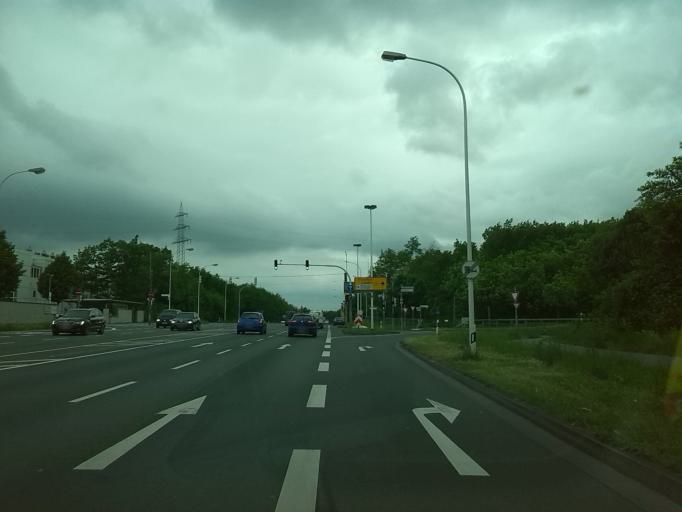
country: DE
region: Hesse
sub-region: Regierungsbezirk Darmstadt
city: Darmstadt
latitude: 49.8906
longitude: 8.6289
